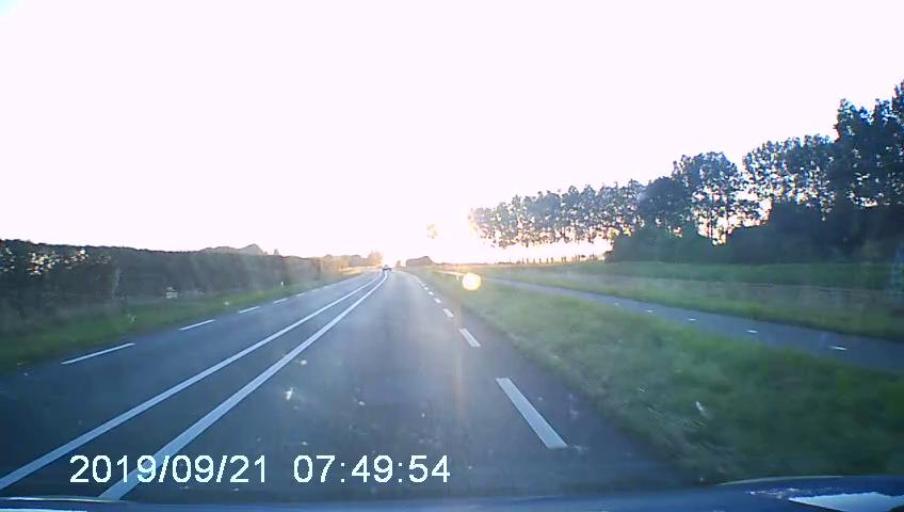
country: NL
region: Zeeland
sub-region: Gemeente Sluis
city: Sluis
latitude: 51.3093
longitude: 3.4570
